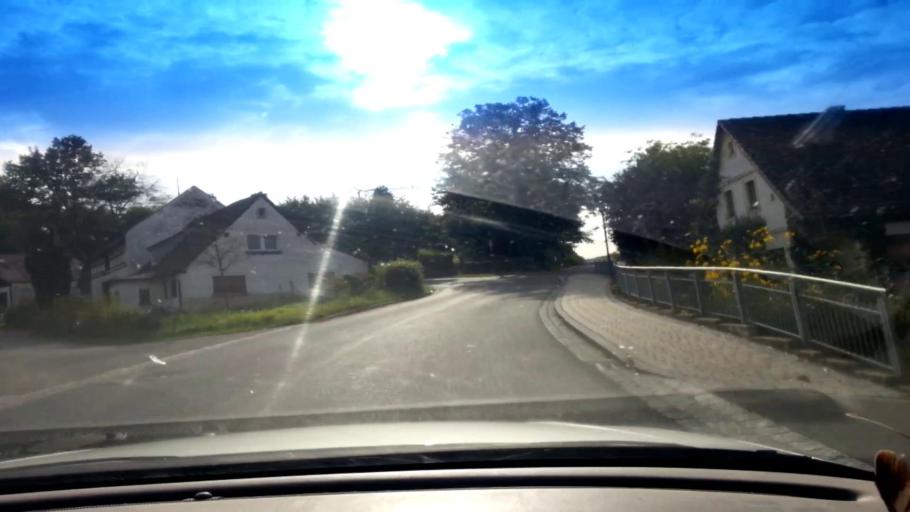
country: DE
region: Bavaria
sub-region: Upper Franconia
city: Buttenheim
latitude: 49.8228
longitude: 11.0252
